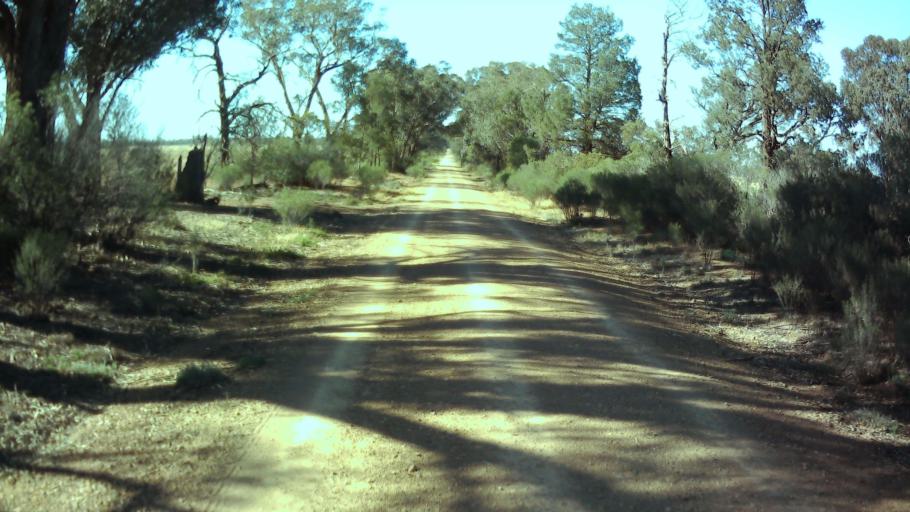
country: AU
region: New South Wales
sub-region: Weddin
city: Grenfell
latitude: -33.9150
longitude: 147.8759
